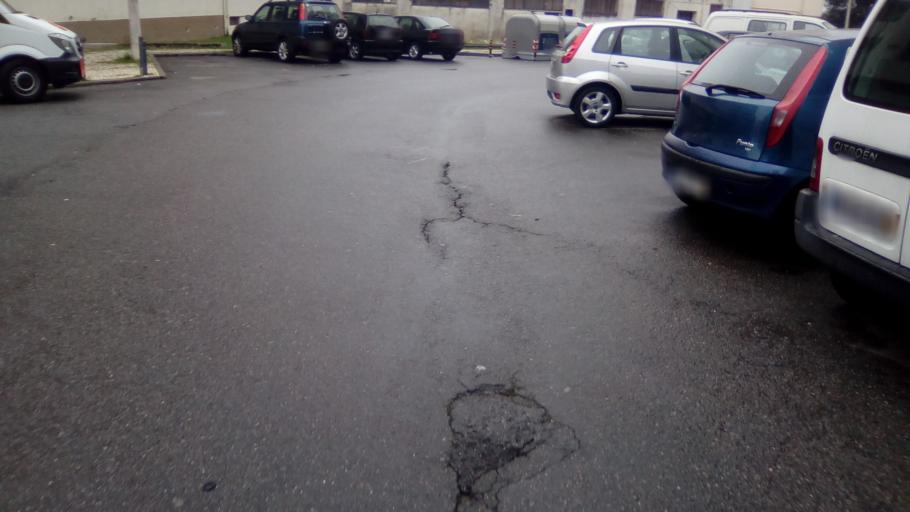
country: PT
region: Braga
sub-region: Braga
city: Braga
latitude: 41.5381
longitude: -8.4272
